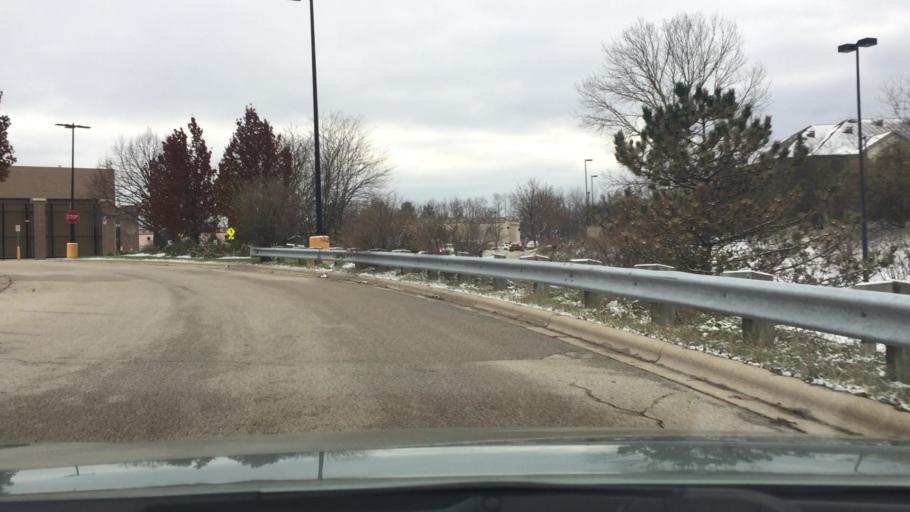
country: US
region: Wisconsin
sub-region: Waukesha County
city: Delafield
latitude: 43.0493
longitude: -88.3707
